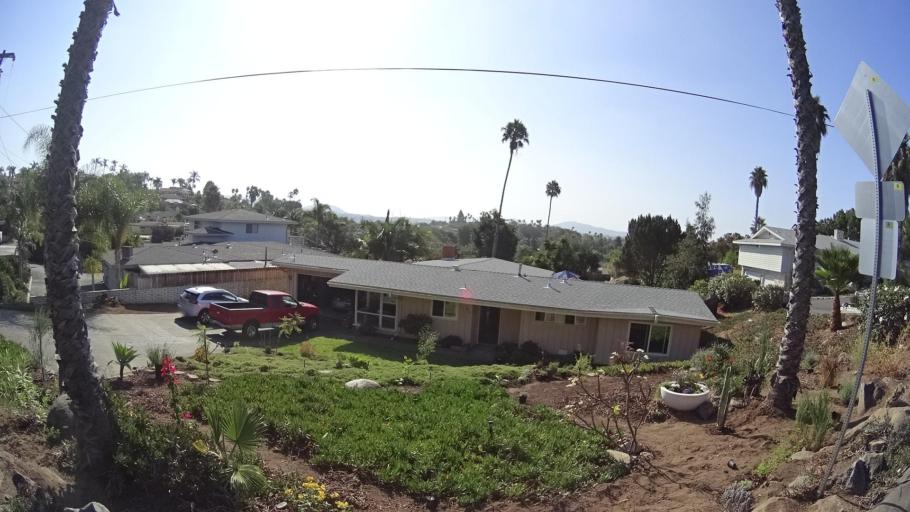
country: US
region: California
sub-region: San Diego County
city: Vista
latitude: 33.1815
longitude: -117.2253
